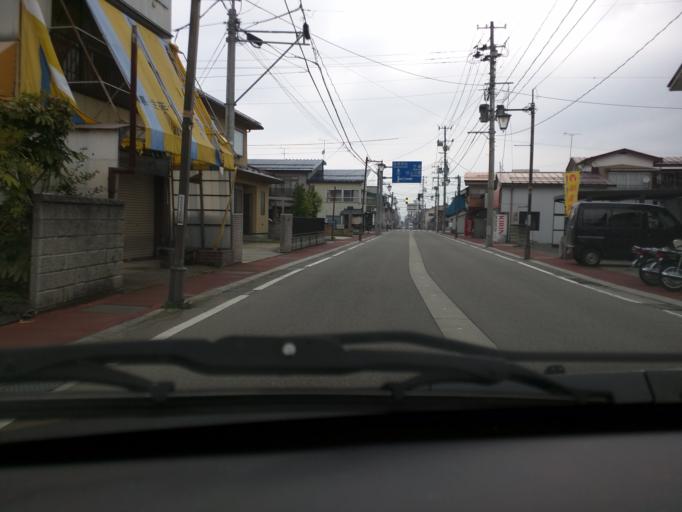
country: JP
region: Fukushima
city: Kitakata
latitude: 37.4570
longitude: 139.8375
